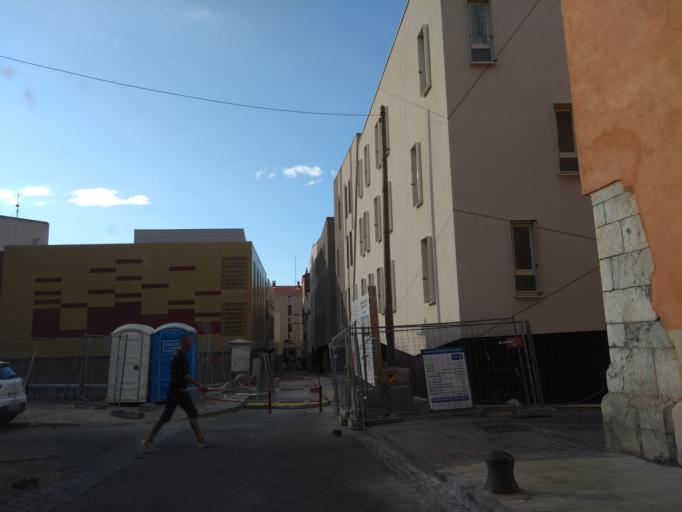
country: FR
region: Languedoc-Roussillon
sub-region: Departement des Pyrenees-Orientales
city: Perpignan
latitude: 42.6947
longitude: 2.8909
